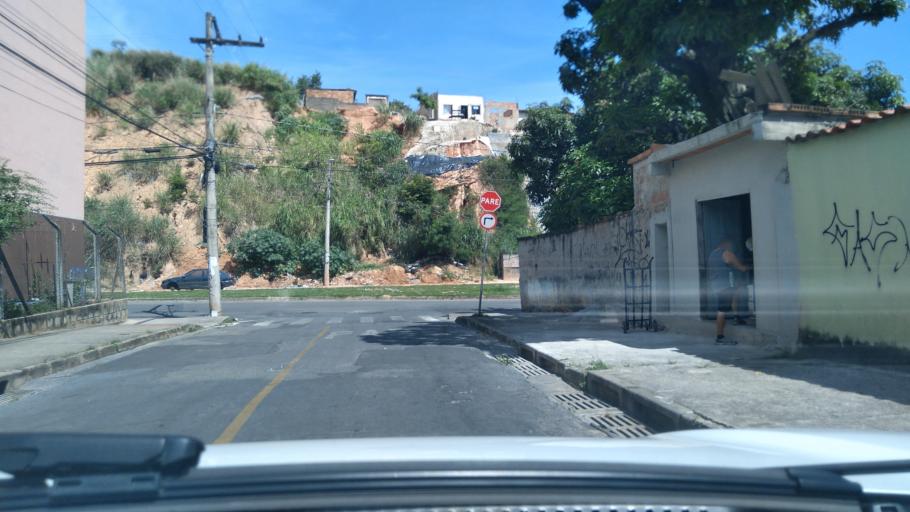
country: BR
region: Minas Gerais
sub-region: Contagem
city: Contagem
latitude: -19.9171
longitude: -44.0049
